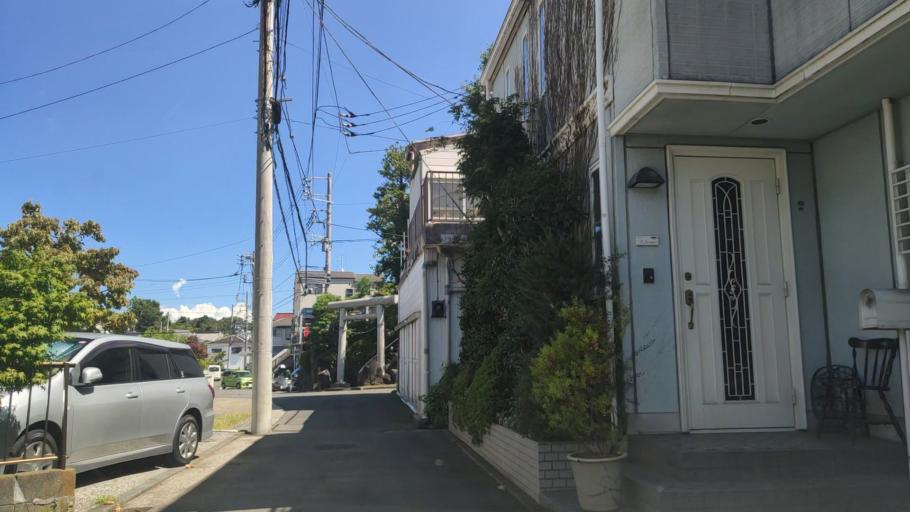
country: JP
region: Kanagawa
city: Yokohama
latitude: 35.5146
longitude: 139.6365
